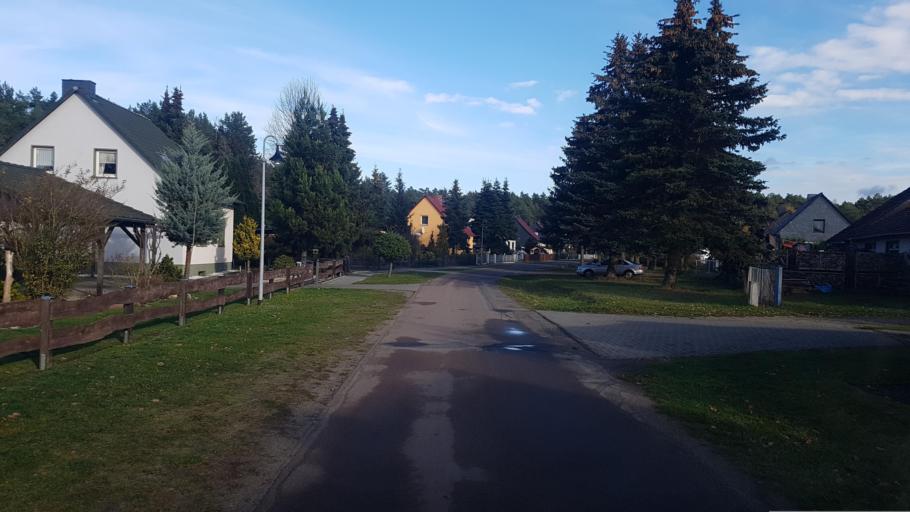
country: DE
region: Brandenburg
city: Wiesenburg
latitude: 52.0691
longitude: 12.4666
